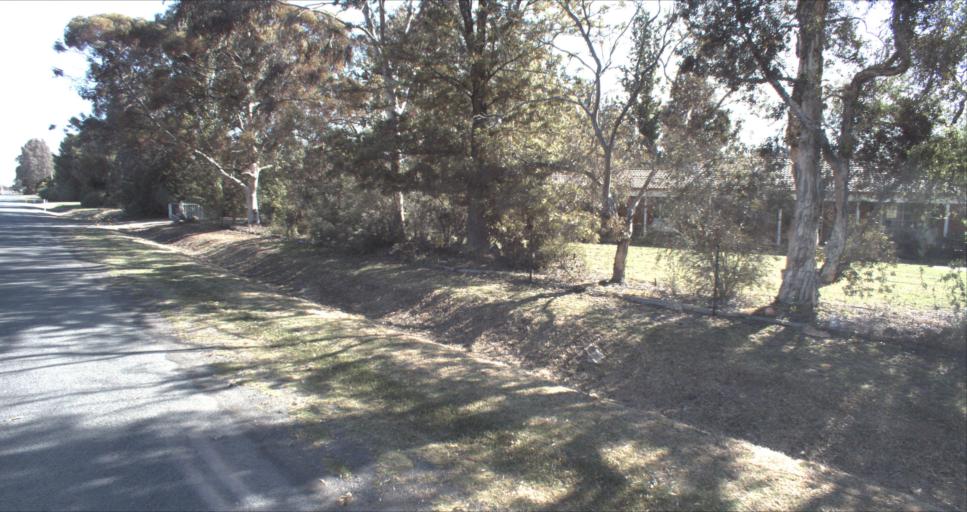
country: AU
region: New South Wales
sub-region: Leeton
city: Leeton
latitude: -34.5417
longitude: 146.4155
